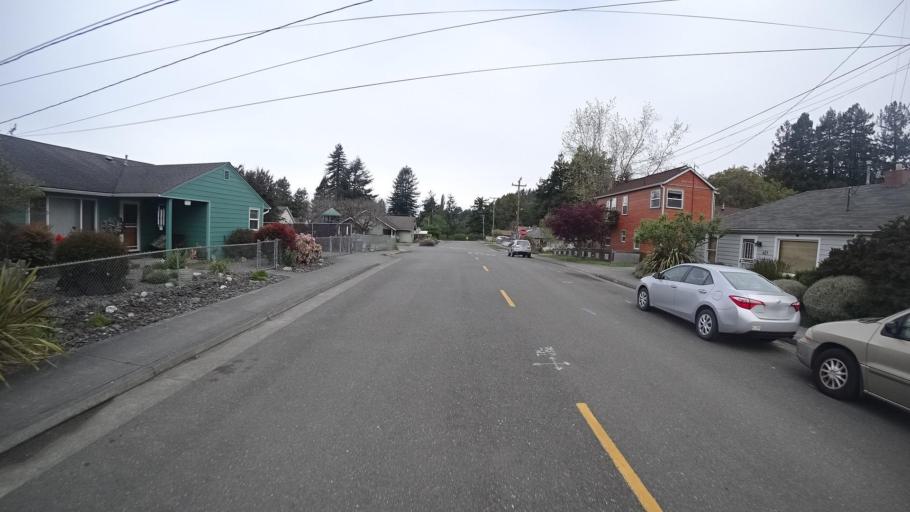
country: US
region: California
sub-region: Humboldt County
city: Blue Lake
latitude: 40.8818
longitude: -123.9852
